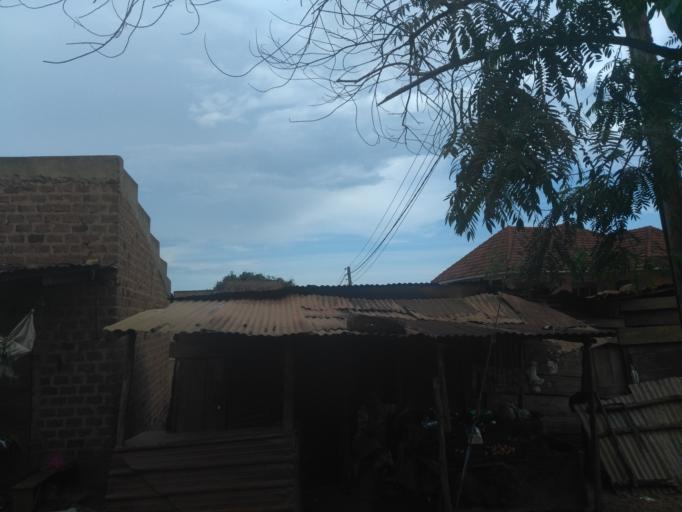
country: UG
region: Central Region
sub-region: Wakiso District
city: Kireka
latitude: 0.3750
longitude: 32.6157
